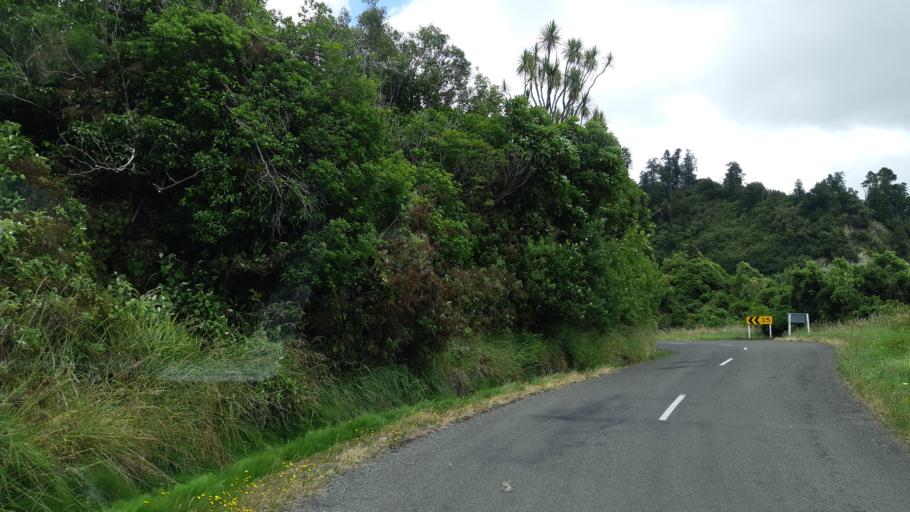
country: NZ
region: Manawatu-Wanganui
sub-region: Palmerston North City
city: Palmerston North
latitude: -39.9394
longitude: 175.9208
